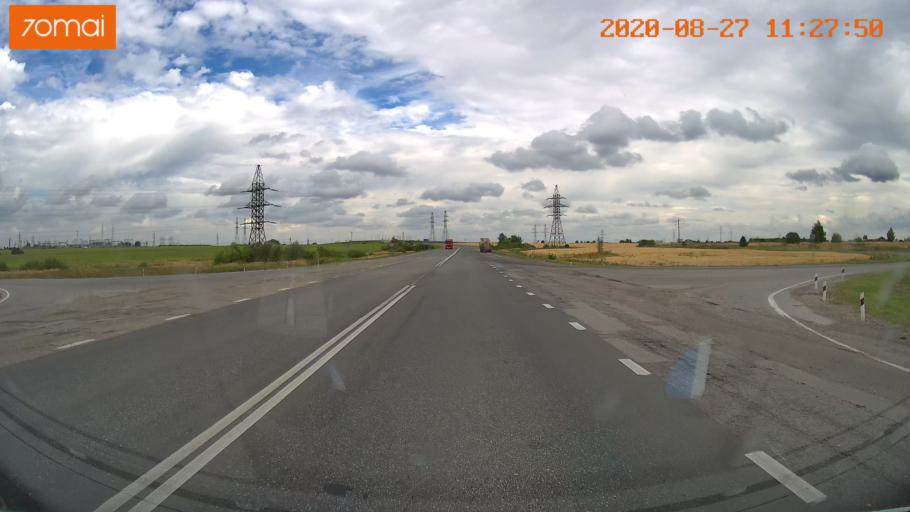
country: RU
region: Rjazan
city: Mikhaylov
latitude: 54.2542
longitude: 38.9973
